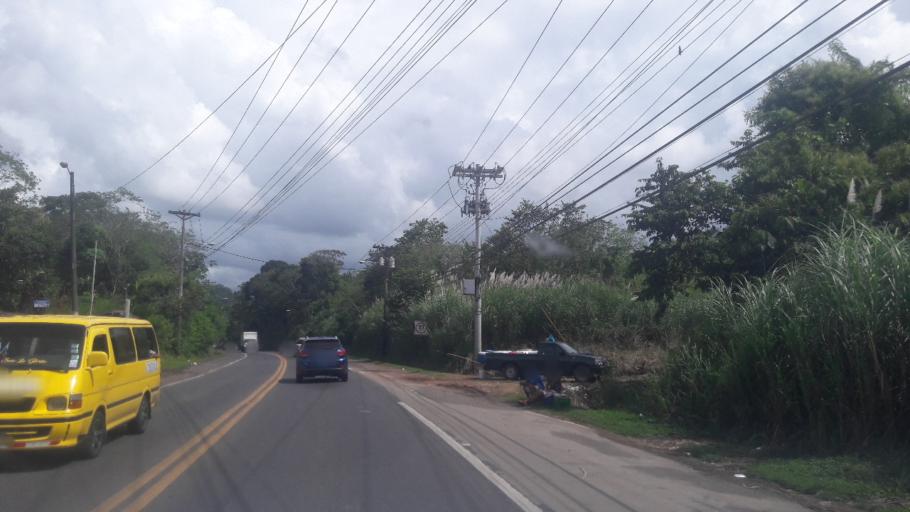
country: PA
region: Panama
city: Alcalde Diaz
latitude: 9.1232
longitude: -79.5918
